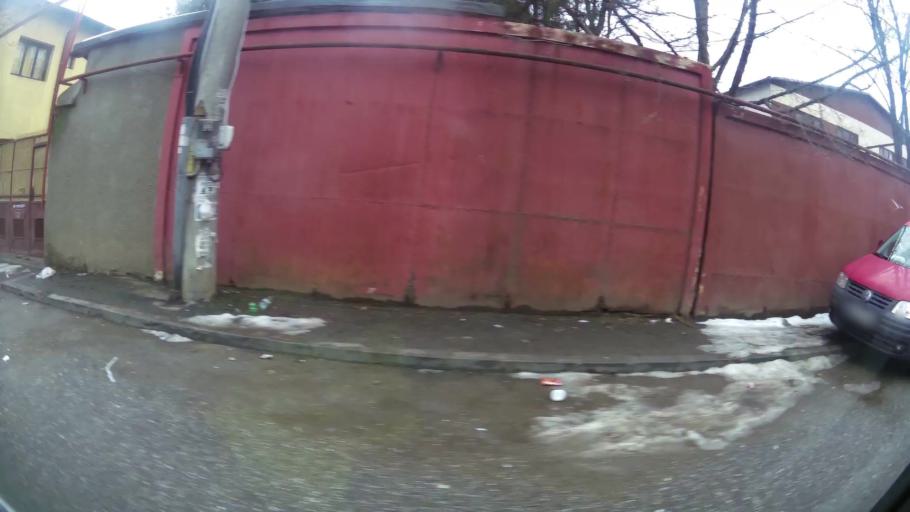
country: RO
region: Ilfov
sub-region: Comuna Popesti-Leordeni
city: Popesti-Leordeni
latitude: 44.4054
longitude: 26.1727
